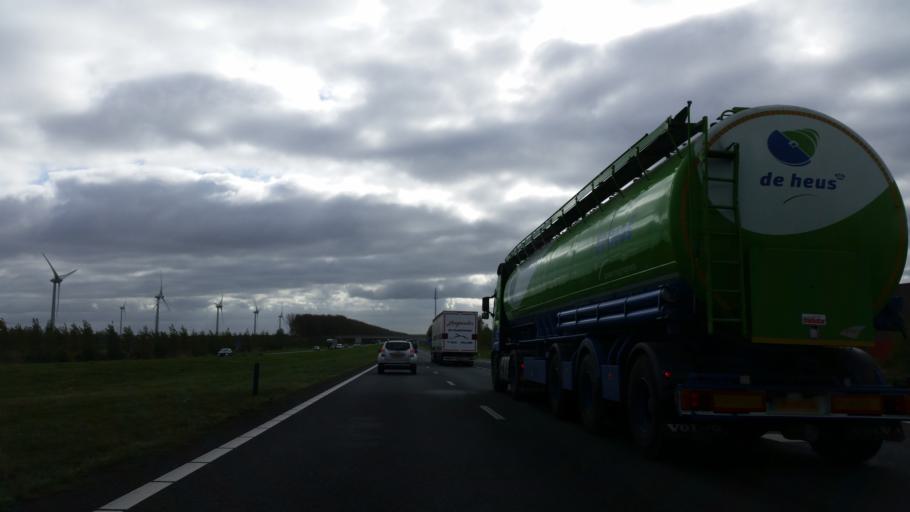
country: NL
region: Flevoland
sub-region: Gemeente Lelystad
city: Lelystad
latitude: 52.5447
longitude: 5.5313
